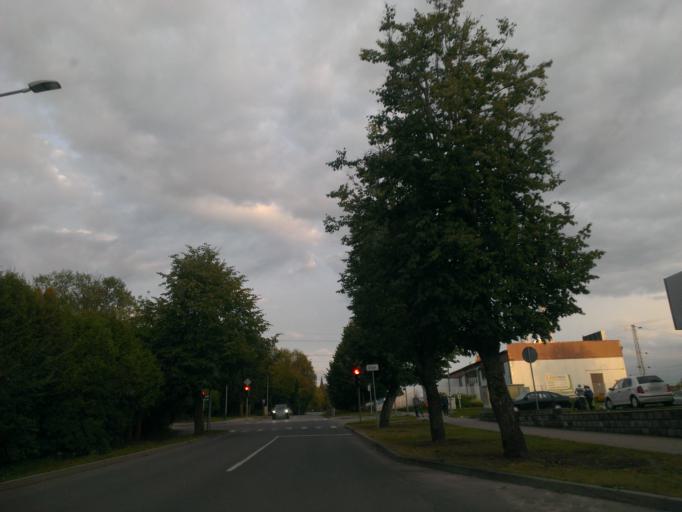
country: LV
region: Ogre
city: Ogre
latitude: 56.8199
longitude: 24.5926
